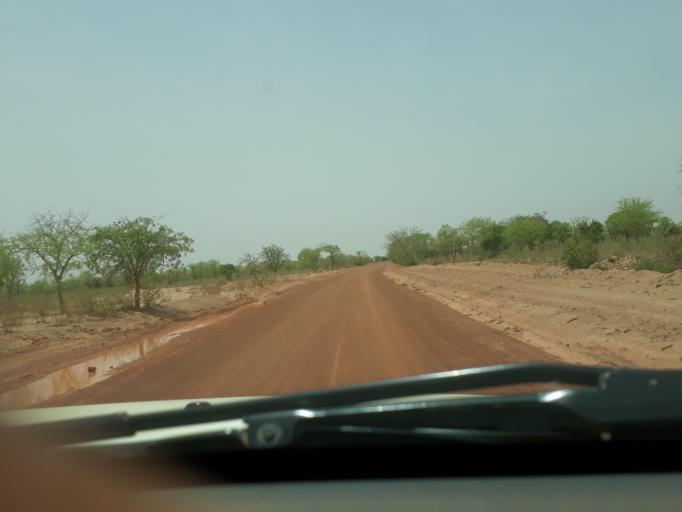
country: BF
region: Plateau-Central
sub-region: Province d'Oubritenga
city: Ziniare
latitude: 12.5805
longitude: -1.3386
